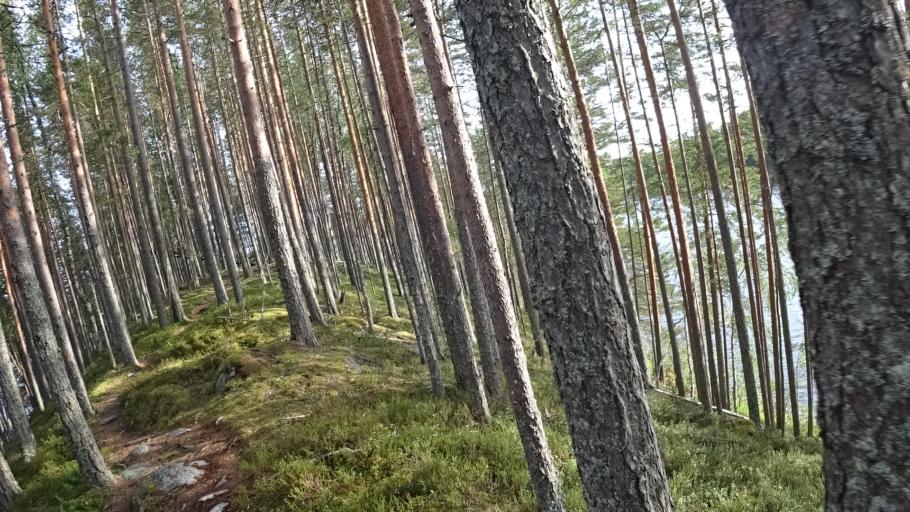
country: FI
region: North Karelia
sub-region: Joensuu
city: Ilomantsi
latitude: 62.5686
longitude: 31.1803
